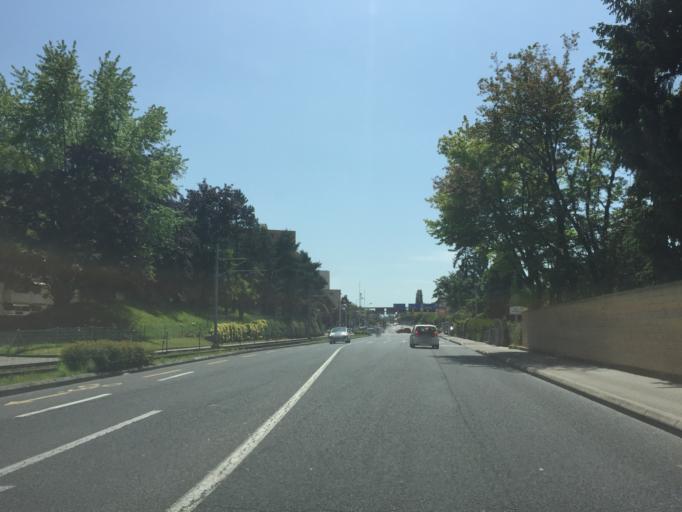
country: CH
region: Vaud
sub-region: Ouest Lausannois District
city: Chavannes
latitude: 46.5301
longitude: 6.5679
